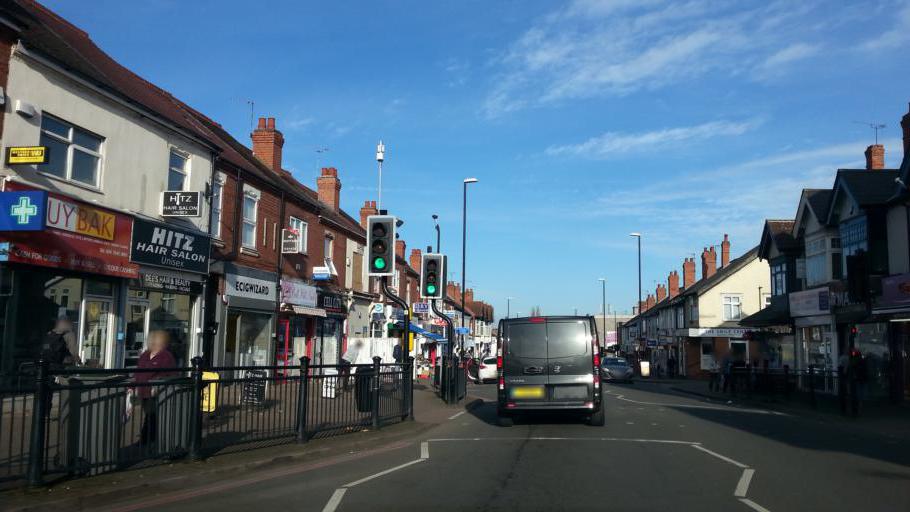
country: GB
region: England
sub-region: Coventry
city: Coventry
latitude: 52.4106
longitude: -1.4839
